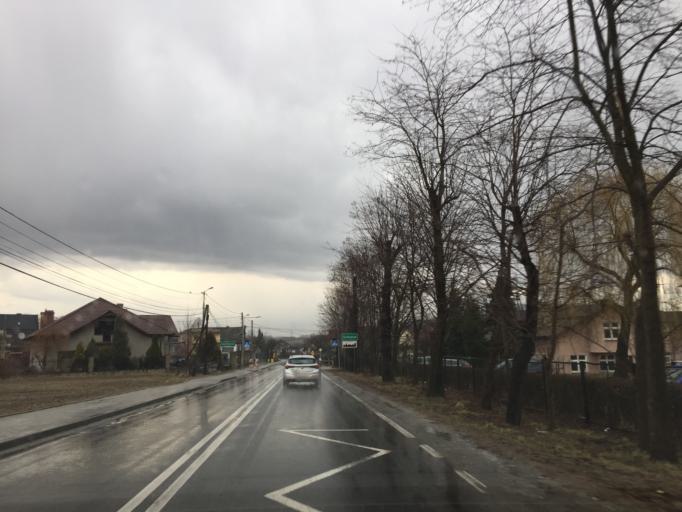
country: PL
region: Lesser Poland Voivodeship
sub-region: Powiat myslenicki
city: Harbutowice
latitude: 49.8230
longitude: 19.7879
